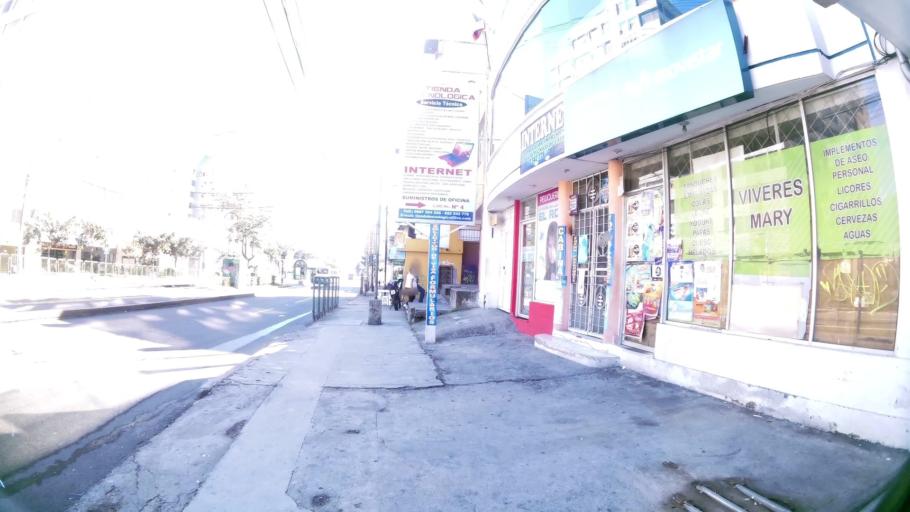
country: US
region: Colorado
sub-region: Mesa County
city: Redlands
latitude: 39.0923
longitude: -108.5903
